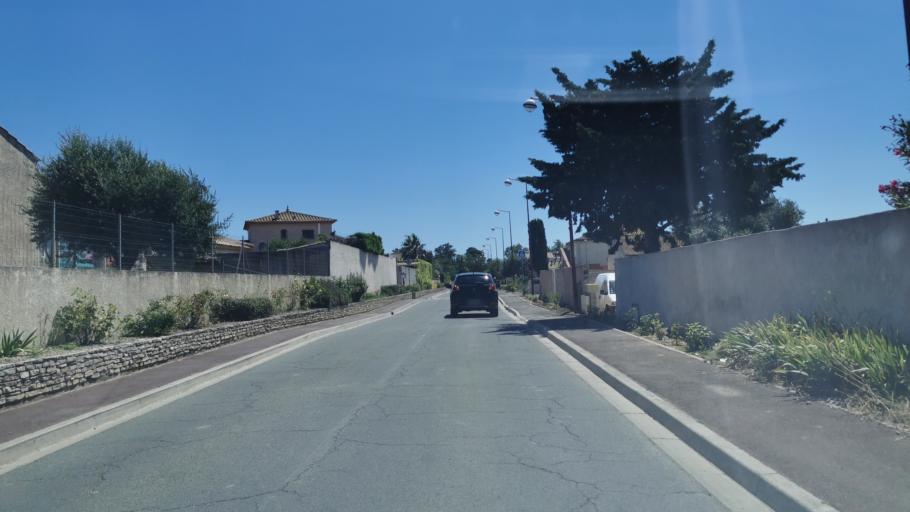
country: FR
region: Languedoc-Roussillon
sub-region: Departement de l'Aude
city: Vinassan
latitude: 43.2090
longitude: 3.0755
